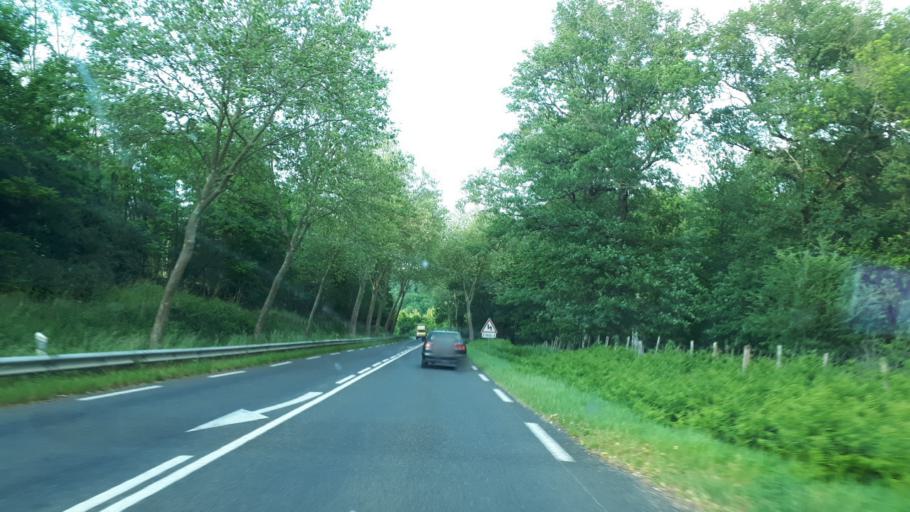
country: FR
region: Centre
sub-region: Departement d'Indre-et-Loire
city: Villedomer
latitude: 47.5444
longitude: 0.8594
